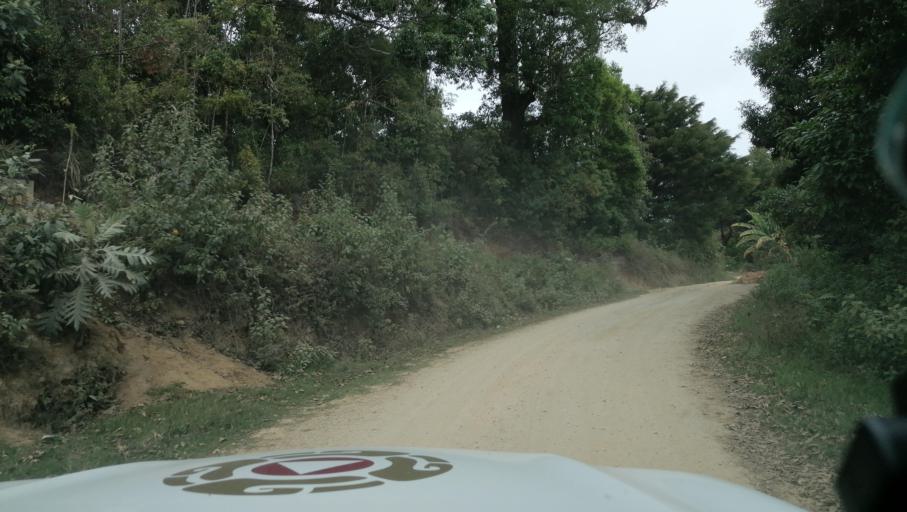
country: MX
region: Chiapas
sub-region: Tapachula
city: Canton Villaflor
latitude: 15.2091
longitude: -92.2401
